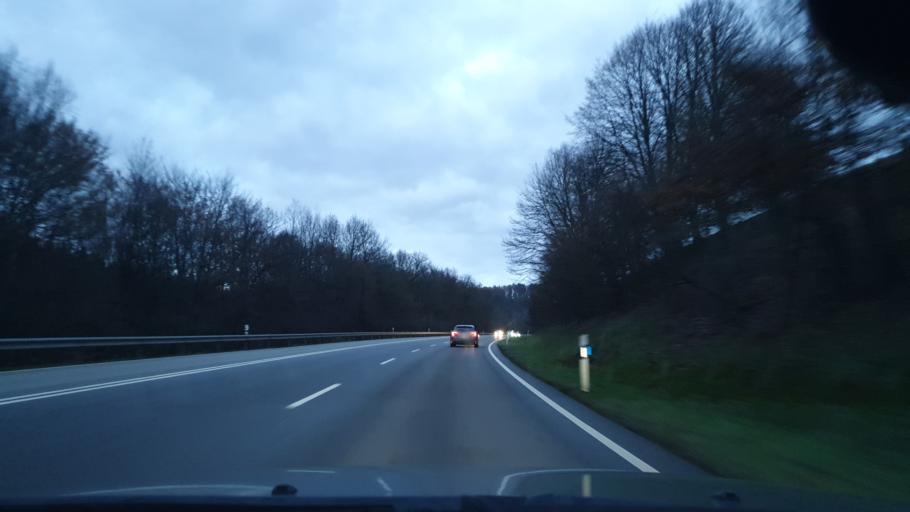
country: DE
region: Rheinland-Pfalz
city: Steinalben
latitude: 49.3059
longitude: 7.6630
